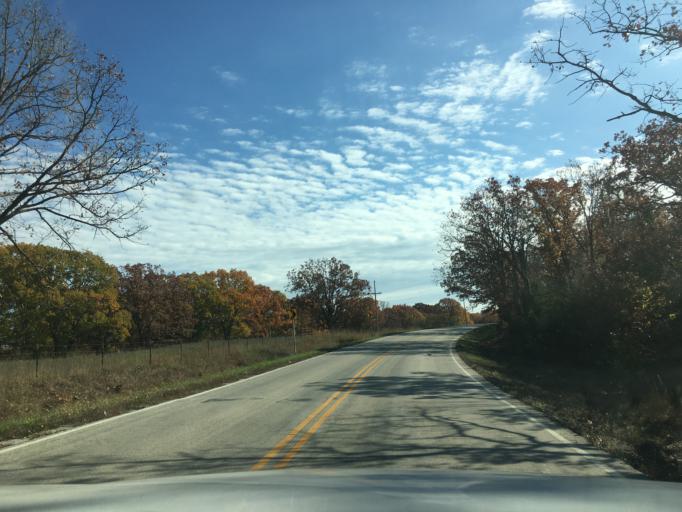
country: US
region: Missouri
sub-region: Maries County
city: Belle
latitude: 38.3081
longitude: -91.7361
